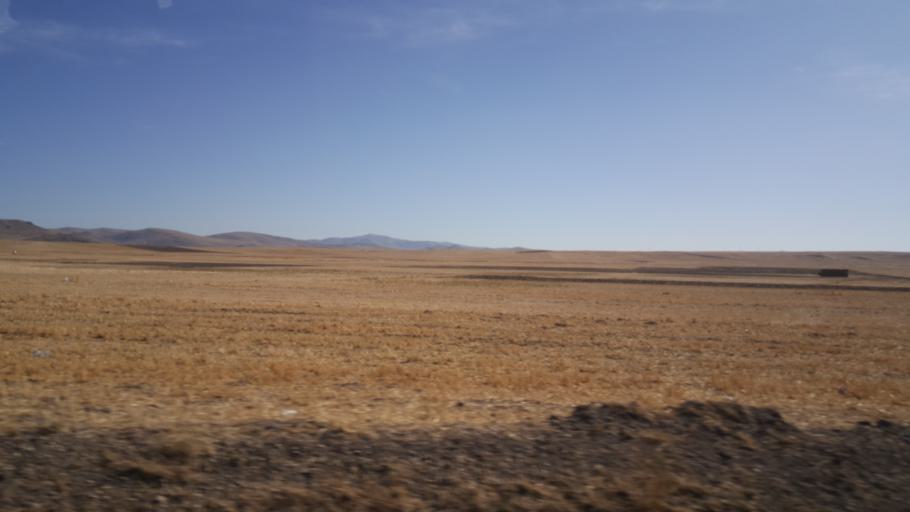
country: TR
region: Ankara
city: Yenice
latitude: 39.3437
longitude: 32.7518
